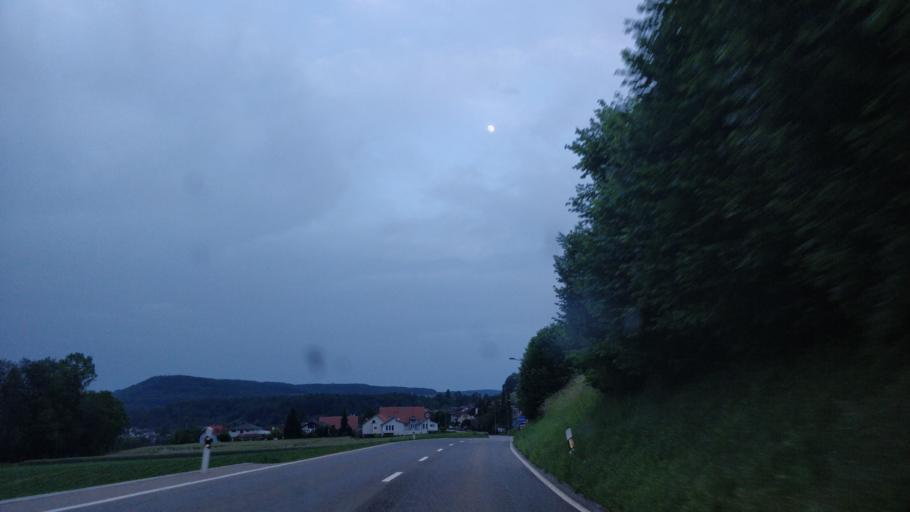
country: CH
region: Zurich
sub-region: Bezirk Buelach
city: Rorbas
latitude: 47.5368
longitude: 8.5675
